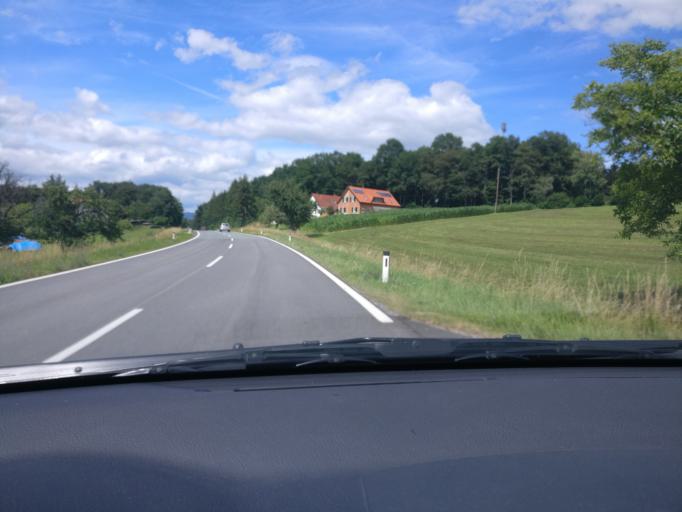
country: AT
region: Styria
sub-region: Politischer Bezirk Hartberg-Fuerstenfeld
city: Kaibing
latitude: 47.2076
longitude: 15.8538
